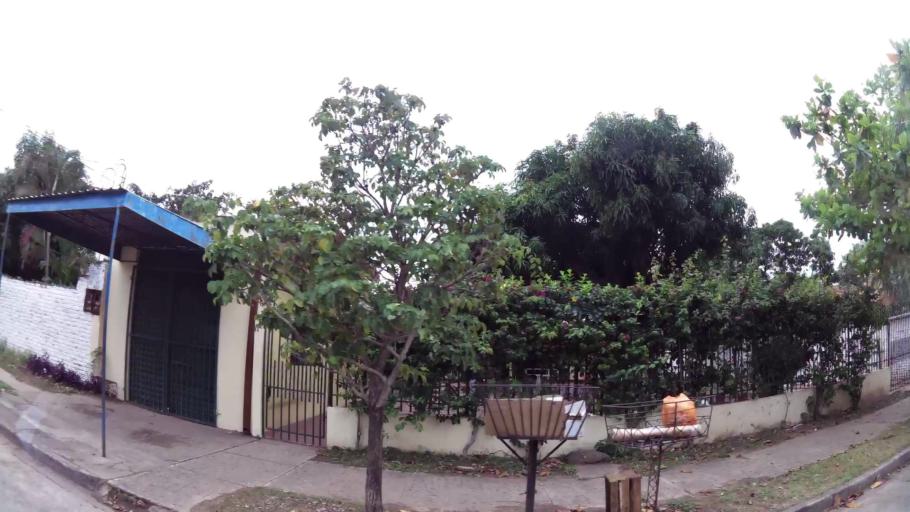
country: BO
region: Santa Cruz
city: Santa Cruz de la Sierra
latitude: -17.7658
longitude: -63.1673
